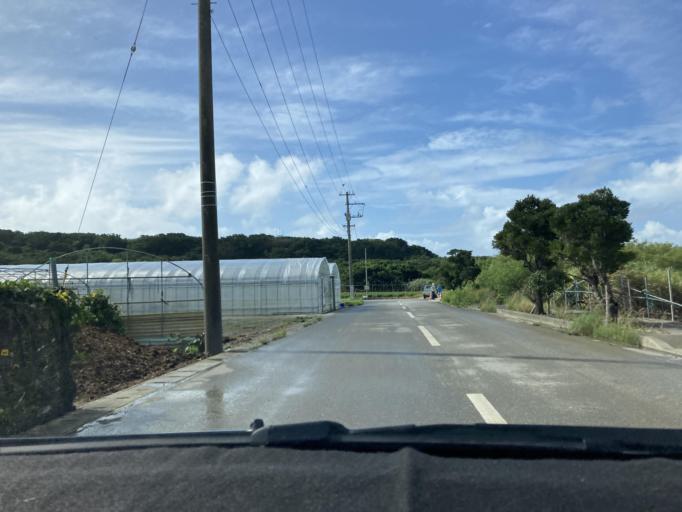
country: JP
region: Okinawa
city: Itoman
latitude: 26.0991
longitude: 127.6613
